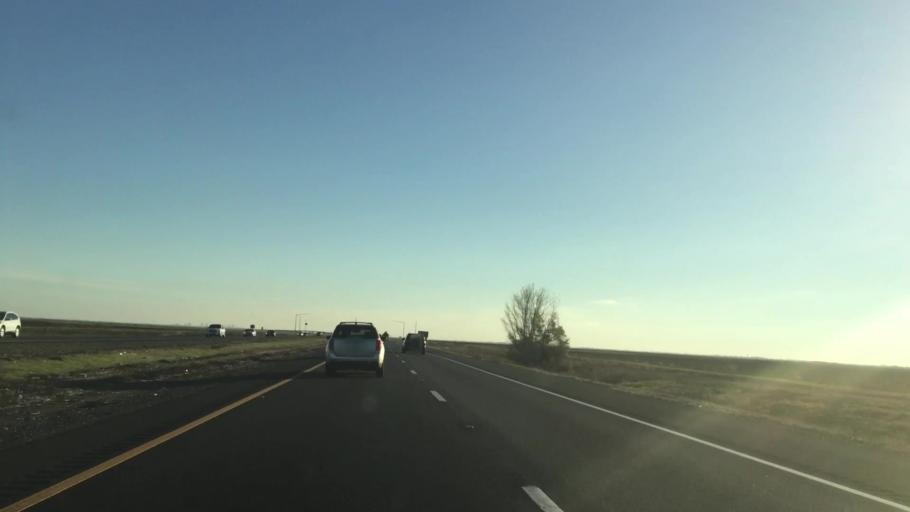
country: US
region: California
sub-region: Sacramento County
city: Elverta
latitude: 38.7841
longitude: -121.5437
